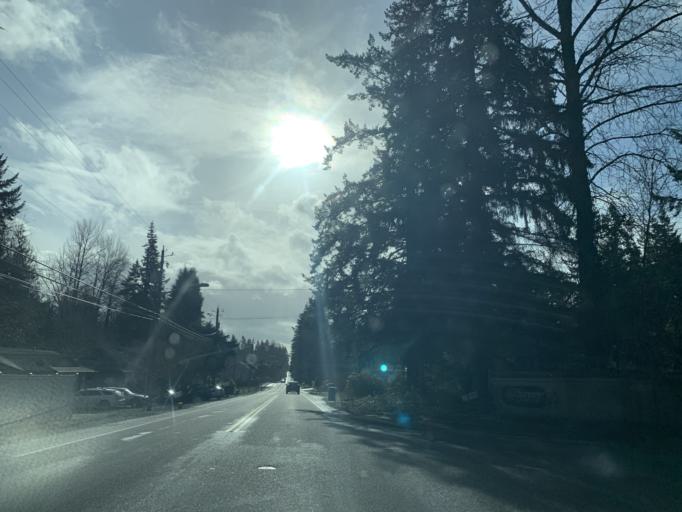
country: US
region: Washington
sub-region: King County
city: Lakeland South
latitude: 47.2831
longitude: -122.2977
